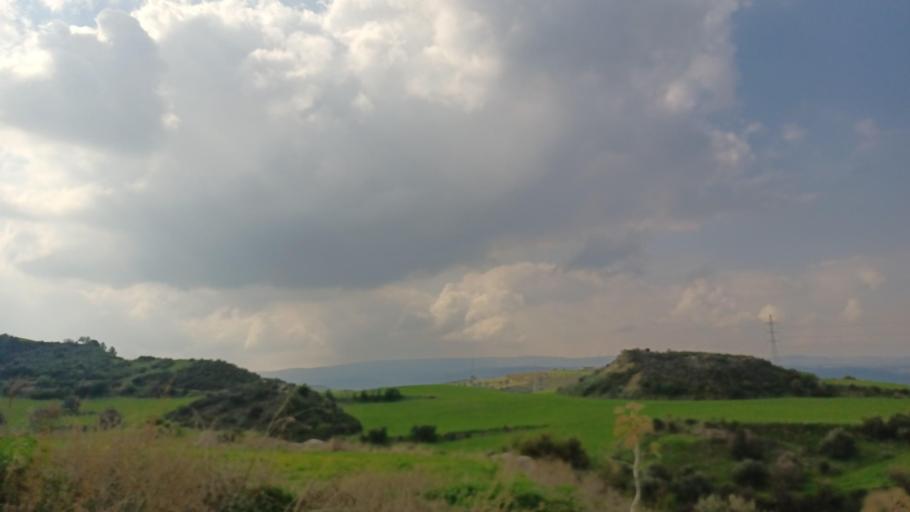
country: CY
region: Pafos
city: Polis
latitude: 35.0388
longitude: 32.4631
